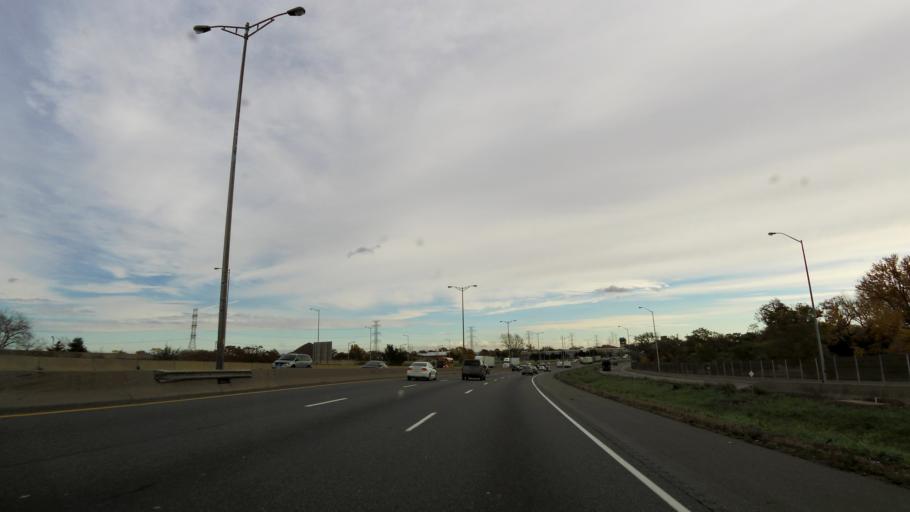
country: CA
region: Ontario
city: Hamilton
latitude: 43.3147
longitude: -79.8069
